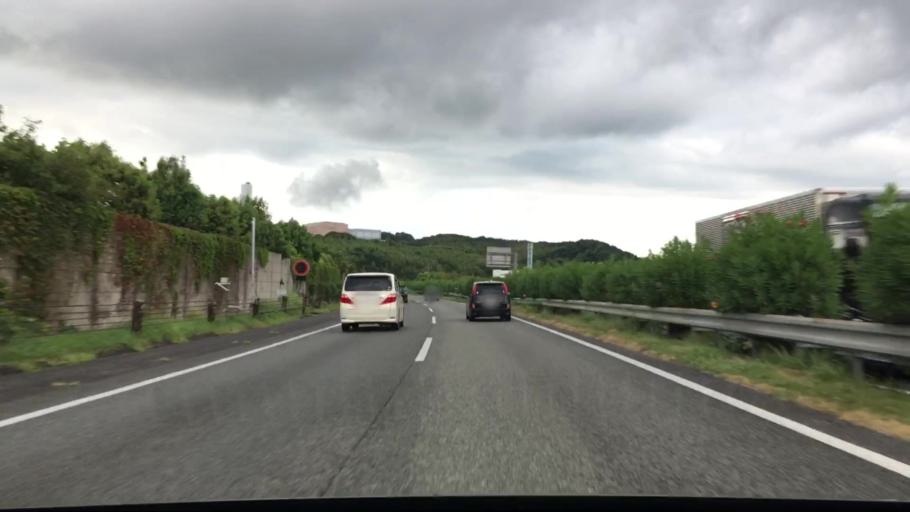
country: JP
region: Fukuoka
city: Sasaguri
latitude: 33.6357
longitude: 130.4907
